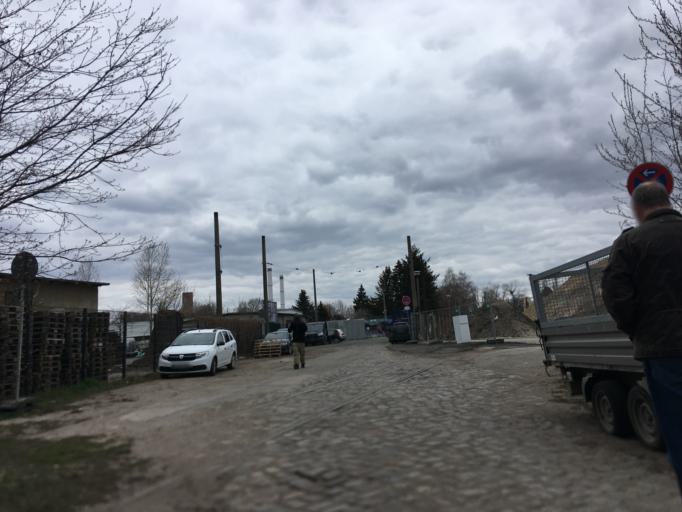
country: DE
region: Berlin
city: Oberschoneweide
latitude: 52.4806
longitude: 13.5084
